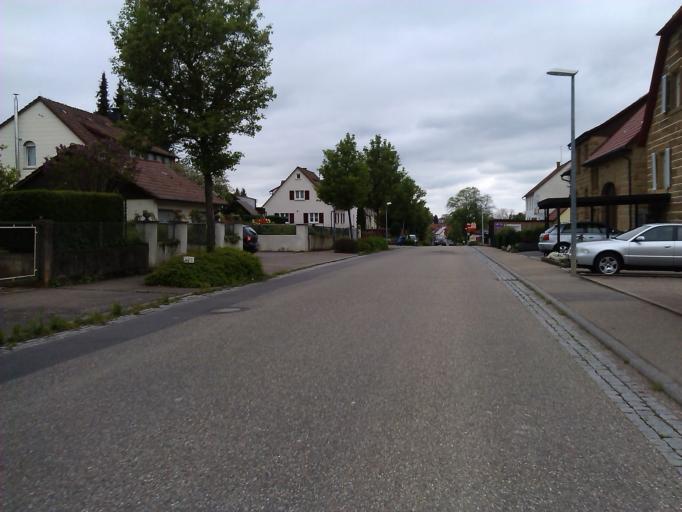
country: DE
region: Baden-Wuerttemberg
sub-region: Karlsruhe Region
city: Oberderdingen
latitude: 49.0598
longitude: 8.8093
